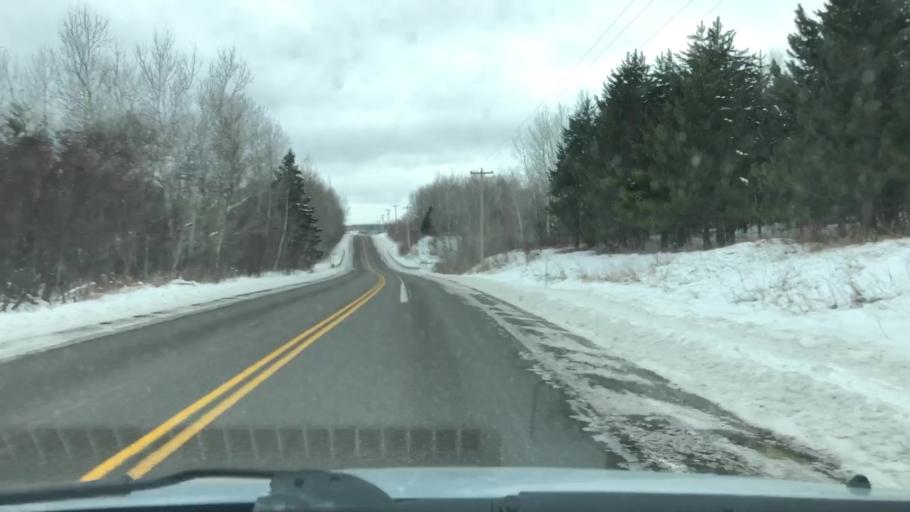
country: US
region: Minnesota
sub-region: Saint Louis County
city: Proctor
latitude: 46.7010
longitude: -92.2840
